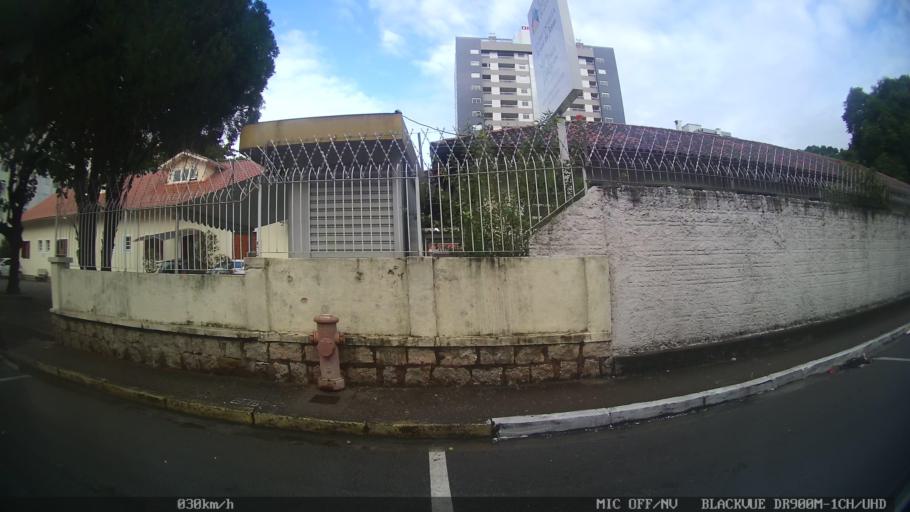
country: BR
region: Santa Catarina
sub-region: Sao Jose
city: Campinas
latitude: -27.5931
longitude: -48.6110
